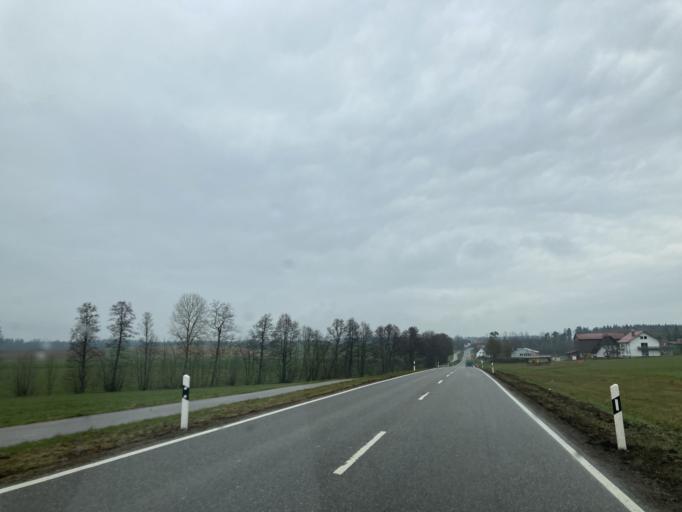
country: DE
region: Baden-Wuerttemberg
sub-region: Freiburg Region
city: Aichhalden
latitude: 48.2482
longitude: 8.4385
